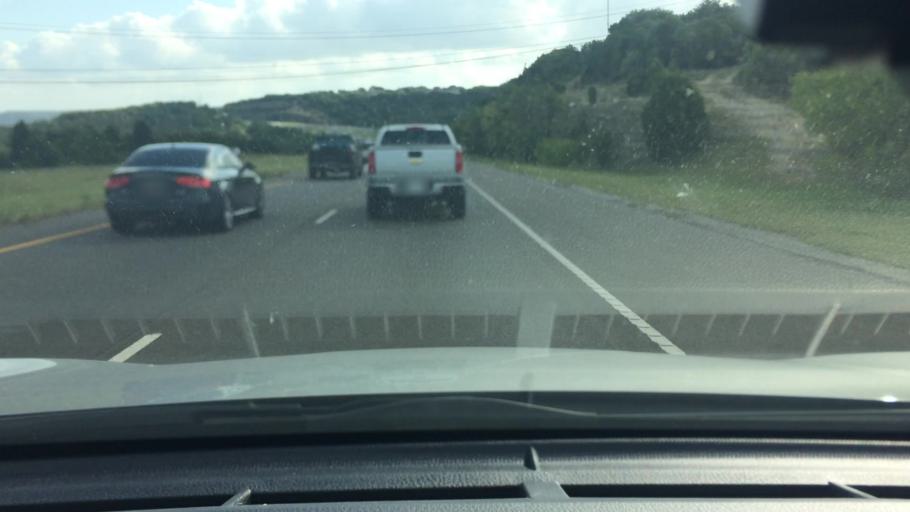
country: US
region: Texas
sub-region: Travis County
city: West Lake Hills
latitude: 30.3191
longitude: -97.8201
